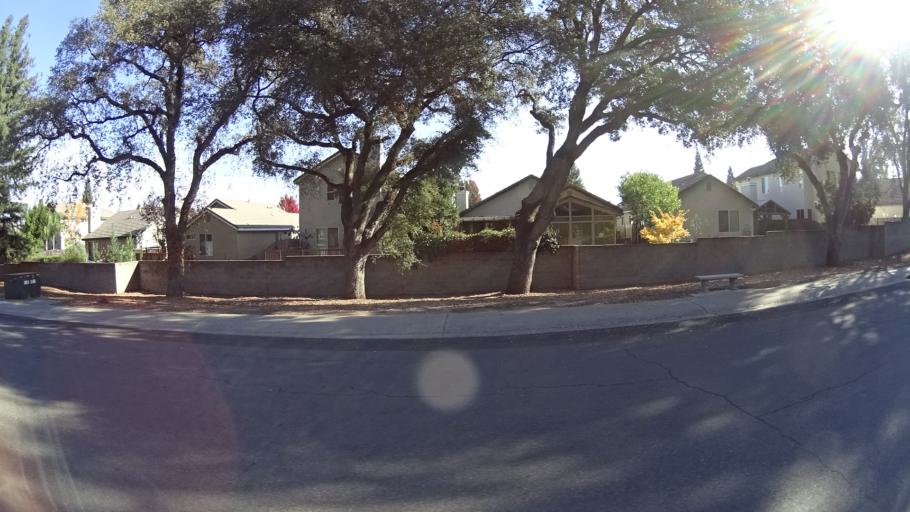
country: US
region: California
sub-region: Sacramento County
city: Citrus Heights
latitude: 38.6828
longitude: -121.2997
